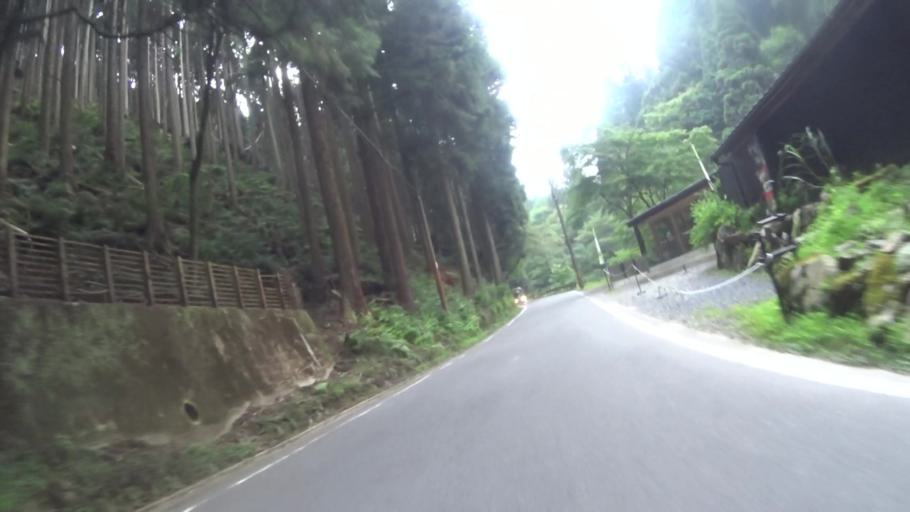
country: JP
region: Kyoto
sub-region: Kyoto-shi
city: Kamigyo-ku
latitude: 35.1134
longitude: 135.7603
